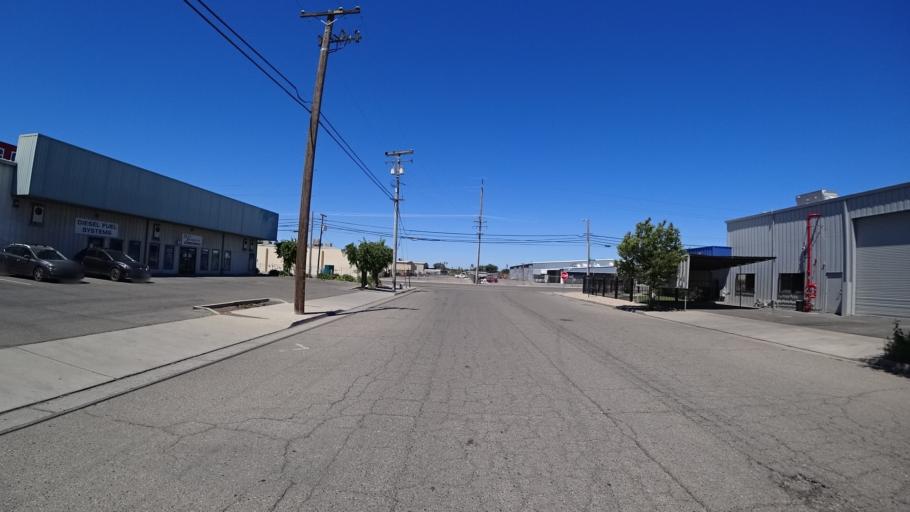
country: US
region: California
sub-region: Fresno County
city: Fresno
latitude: 36.7041
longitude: -119.7812
